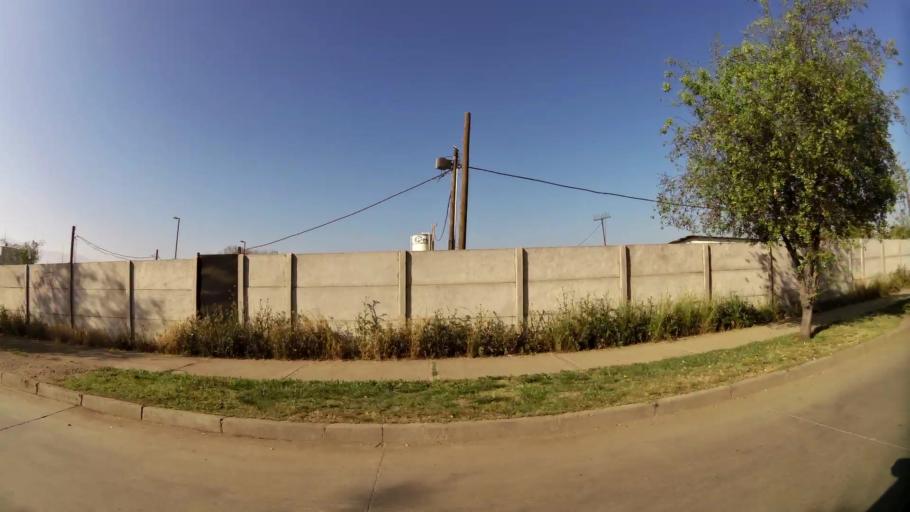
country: CL
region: Santiago Metropolitan
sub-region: Provincia de Chacabuco
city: Chicureo Abajo
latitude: -33.3665
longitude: -70.6679
